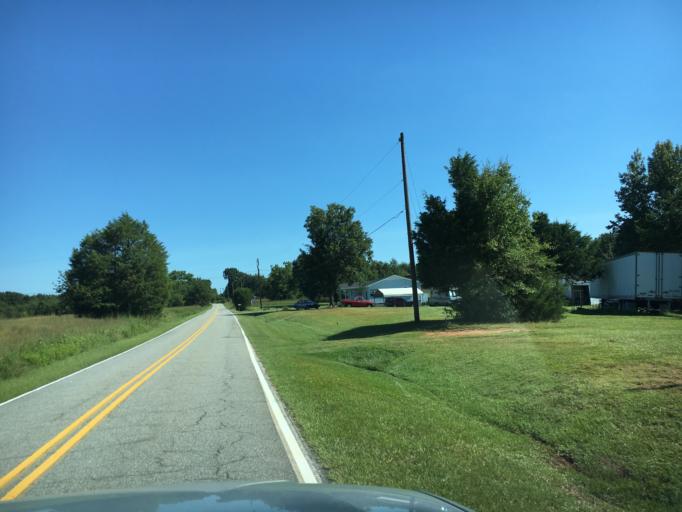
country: US
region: South Carolina
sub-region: Greenville County
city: Five Forks
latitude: 34.8555
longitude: -82.1628
